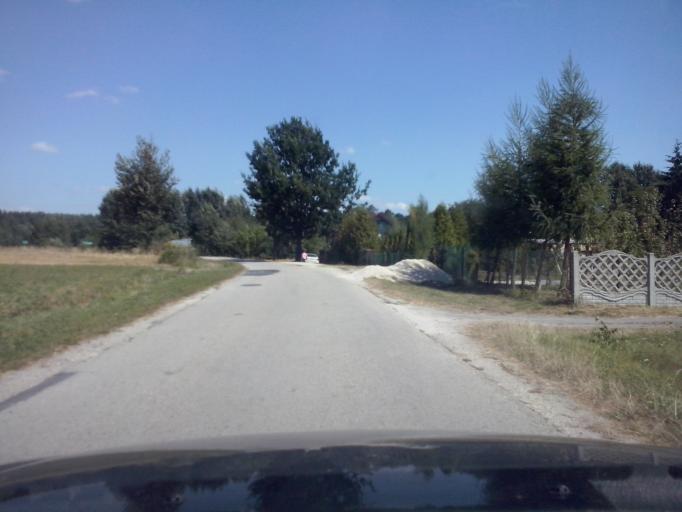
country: PL
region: Swietokrzyskie
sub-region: Powiat buski
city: Gnojno
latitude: 50.6015
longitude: 20.8913
